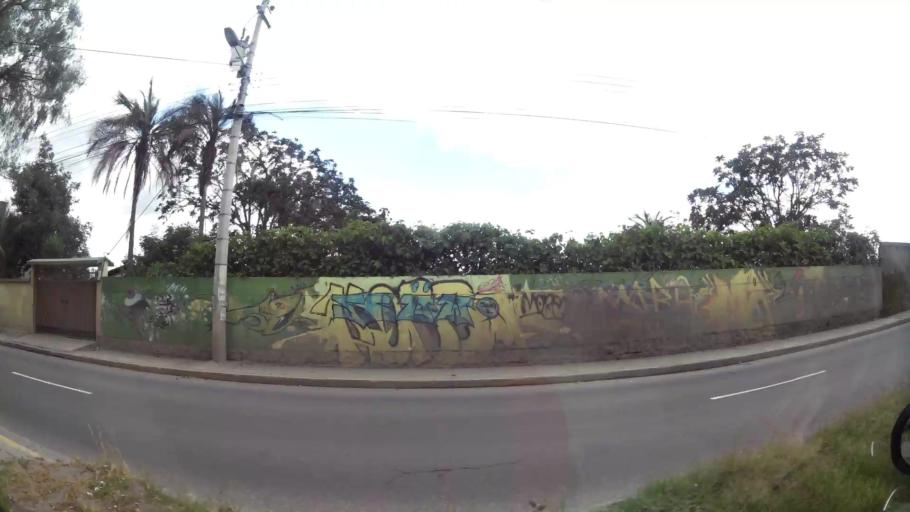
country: EC
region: Pichincha
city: Quito
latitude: -0.0874
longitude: -78.4247
